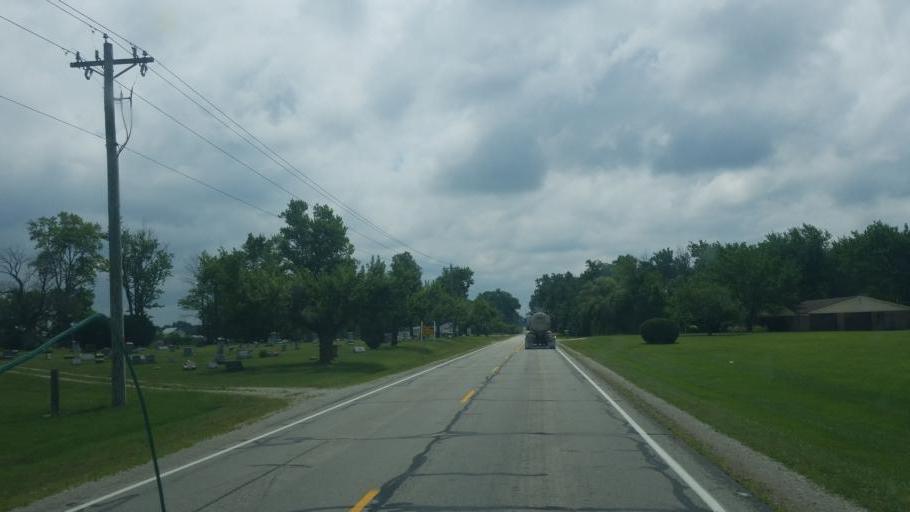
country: US
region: Indiana
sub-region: Huntington County
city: Warren
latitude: 40.6712
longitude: -85.4142
